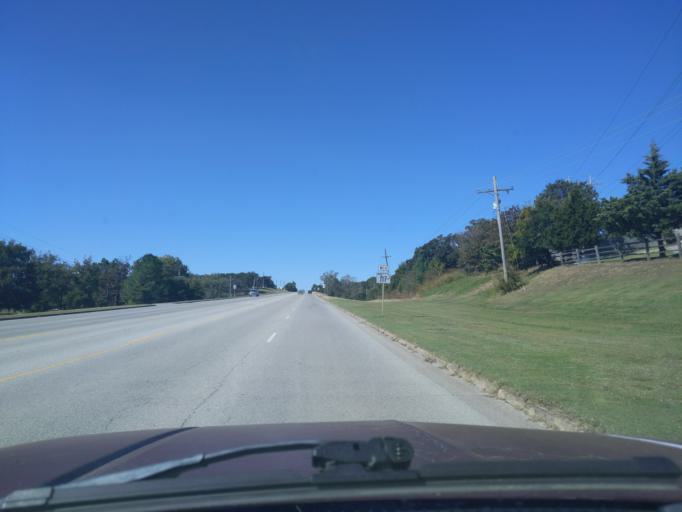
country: US
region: Oklahoma
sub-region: Tulsa County
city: Glenpool
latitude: 35.9885
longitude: -96.0364
